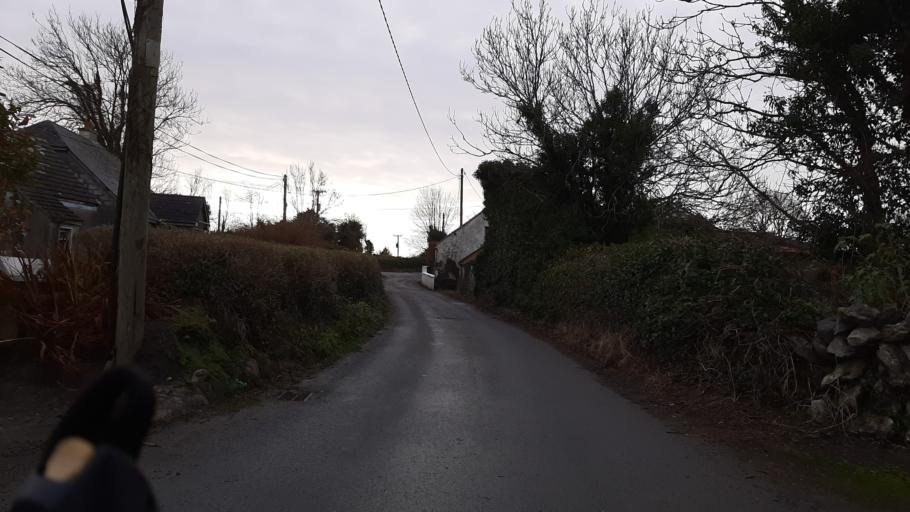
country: IE
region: Connaught
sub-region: County Galway
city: Gaillimh
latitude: 53.3055
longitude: -9.0723
